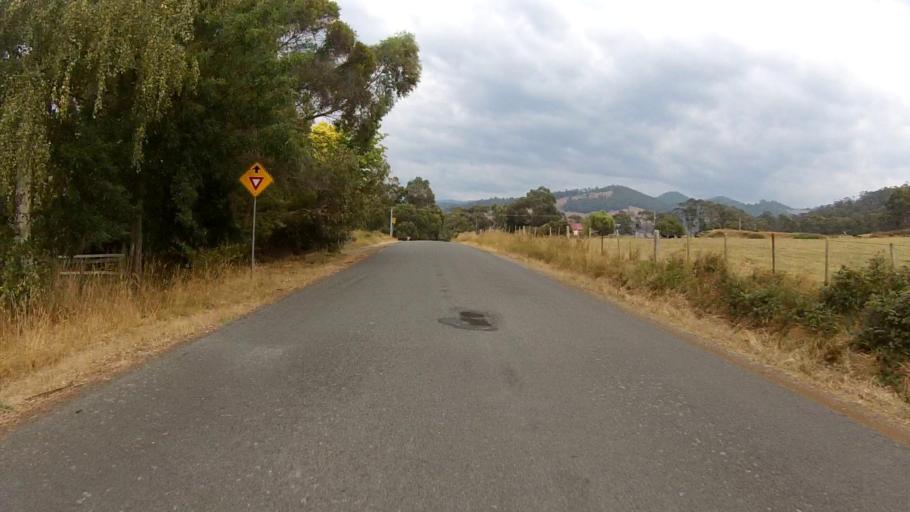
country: AU
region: Tasmania
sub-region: Huon Valley
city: Cygnet
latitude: -43.1838
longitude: 147.1090
